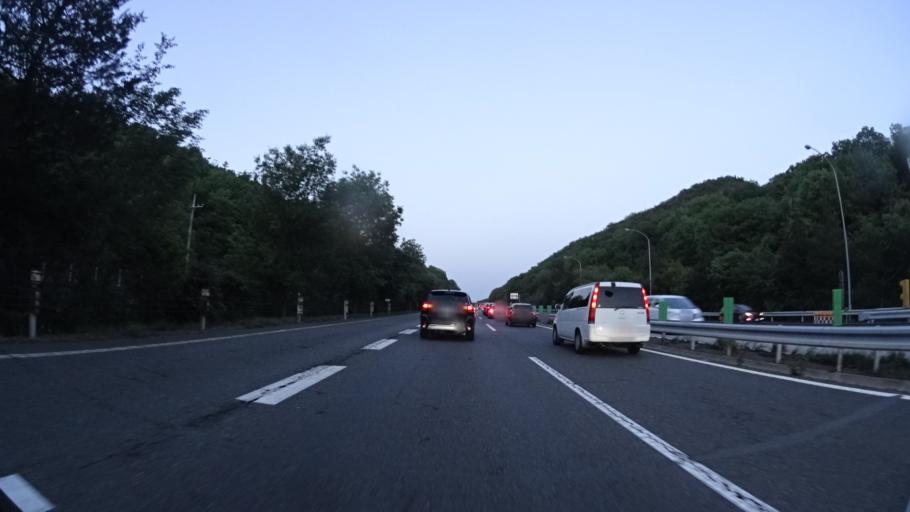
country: JP
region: Hyogo
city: Kariya
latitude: 34.7838
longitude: 134.2669
